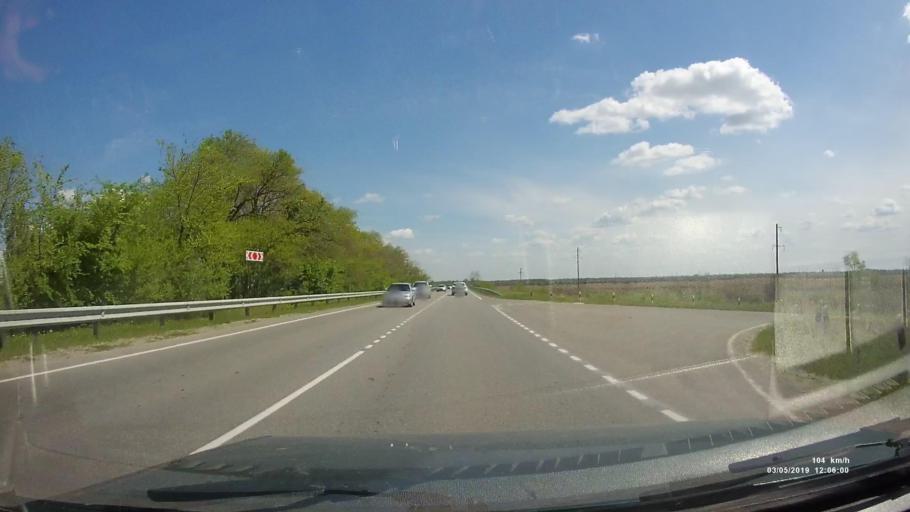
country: RU
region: Rostov
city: Bagayevskaya
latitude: 47.2862
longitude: 40.4417
